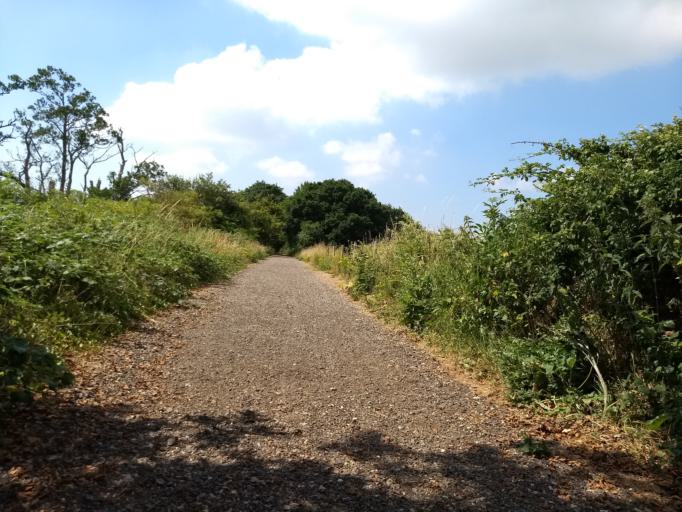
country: GB
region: England
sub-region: Isle of Wight
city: Brading
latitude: 50.6850
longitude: -1.1292
